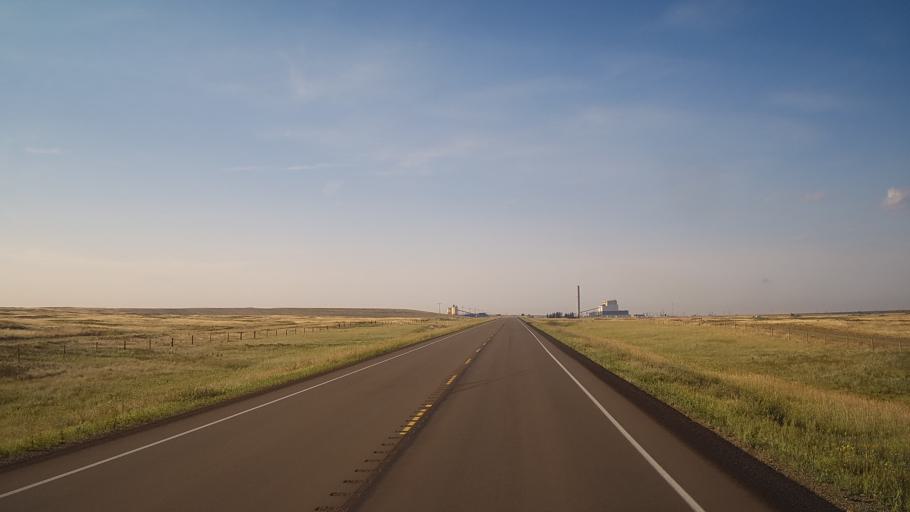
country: CA
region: Alberta
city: Hanna
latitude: 51.4710
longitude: -111.7865
